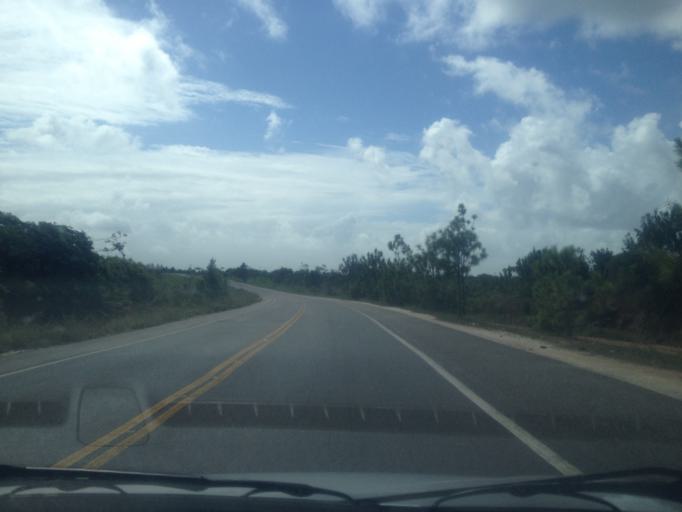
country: BR
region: Bahia
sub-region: Conde
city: Conde
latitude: -11.8679
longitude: -37.6321
